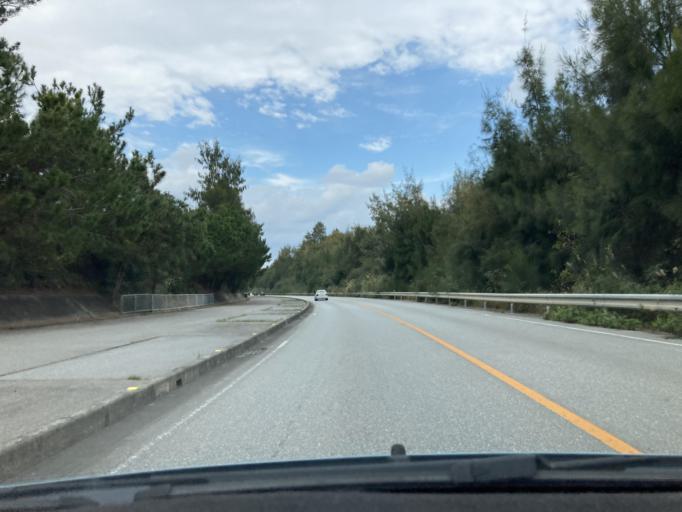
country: JP
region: Okinawa
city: Ishikawa
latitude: 26.4857
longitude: 127.8536
